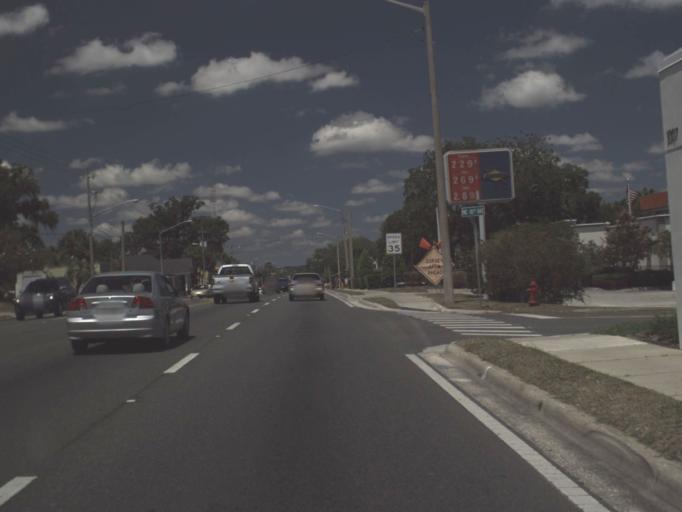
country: US
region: Florida
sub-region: Marion County
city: Ocala
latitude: 29.1871
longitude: -82.1262
